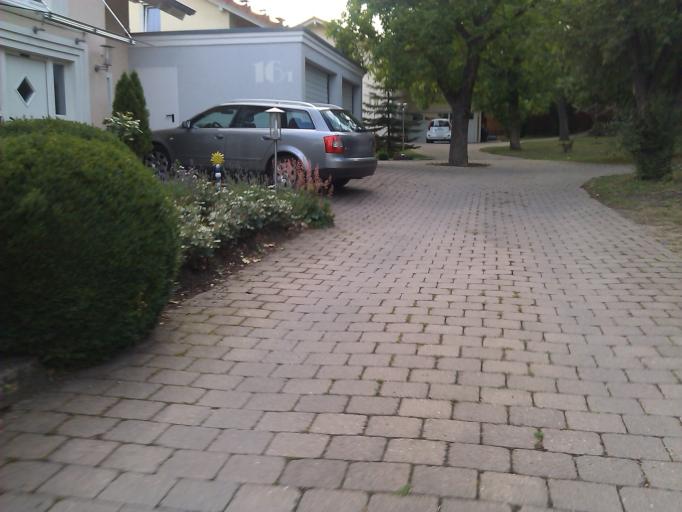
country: DE
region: Baden-Wuerttemberg
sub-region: Regierungsbezirk Stuttgart
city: Untereisesheim
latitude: 49.2303
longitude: 9.1970
